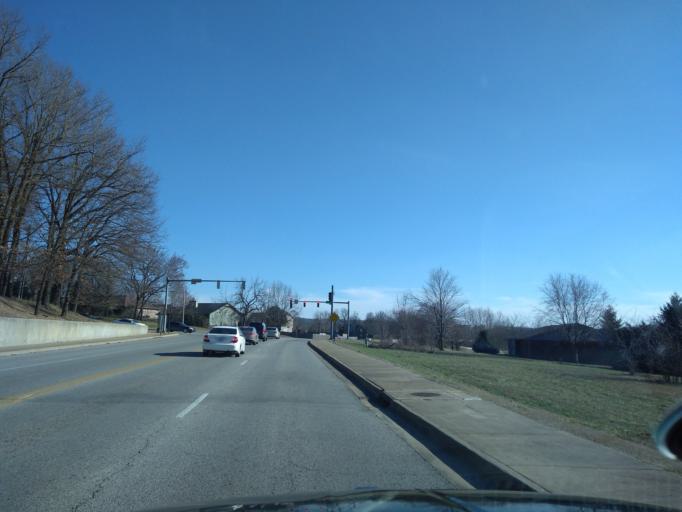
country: US
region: Arkansas
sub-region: Washington County
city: Johnson
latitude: 36.1260
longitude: -94.1626
